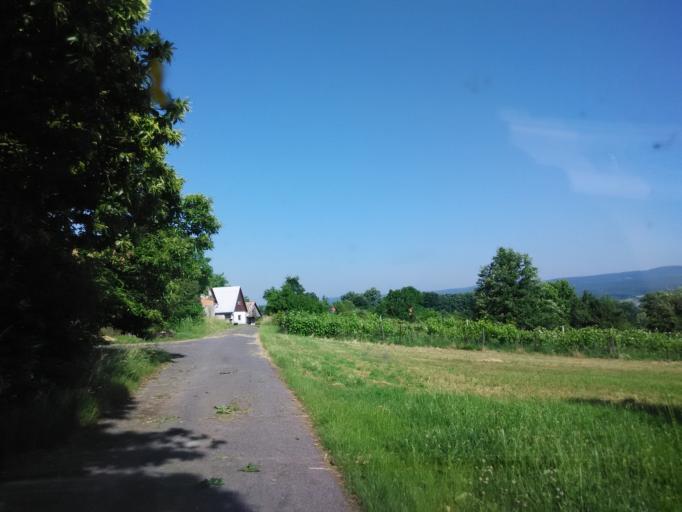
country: SK
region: Nitriansky
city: Levice
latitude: 48.2765
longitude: 18.6798
